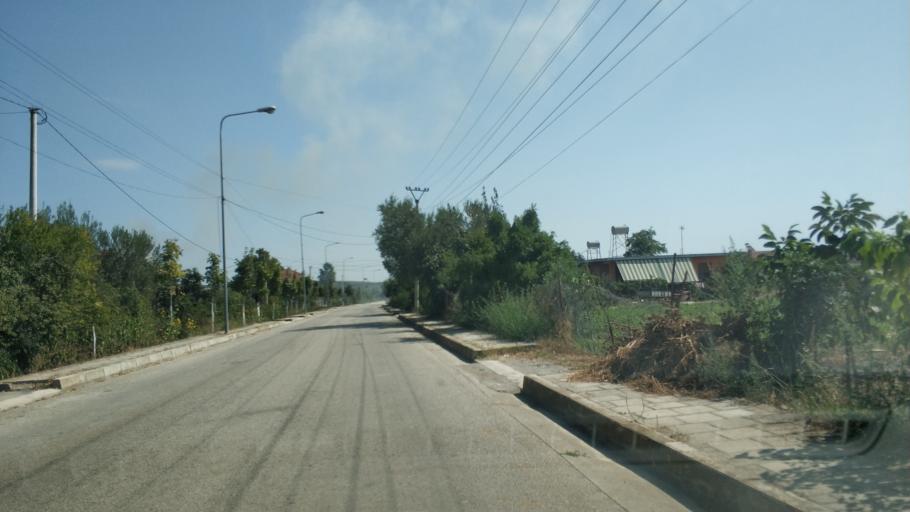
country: AL
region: Fier
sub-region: Rrethi i Lushnjes
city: Divjake
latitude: 41.0026
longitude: 19.5256
